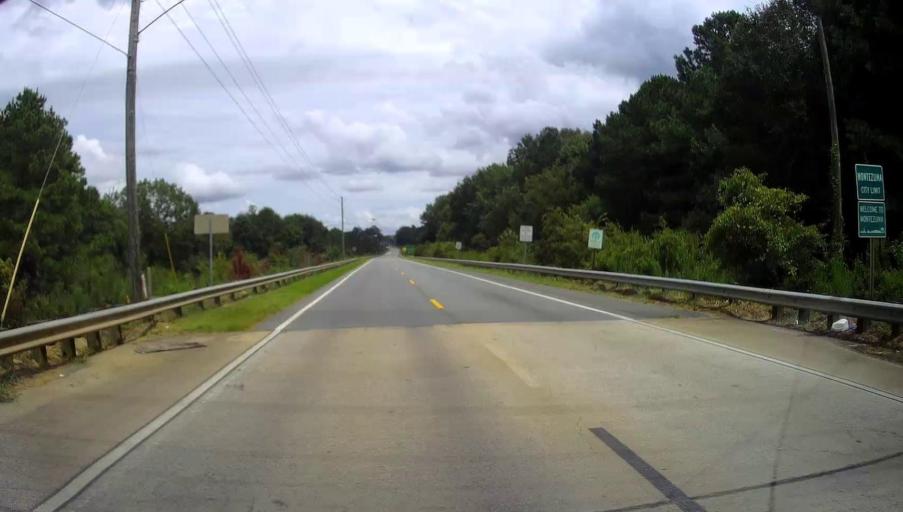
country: US
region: Georgia
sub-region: Macon County
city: Montezuma
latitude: 32.2931
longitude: -84.0408
